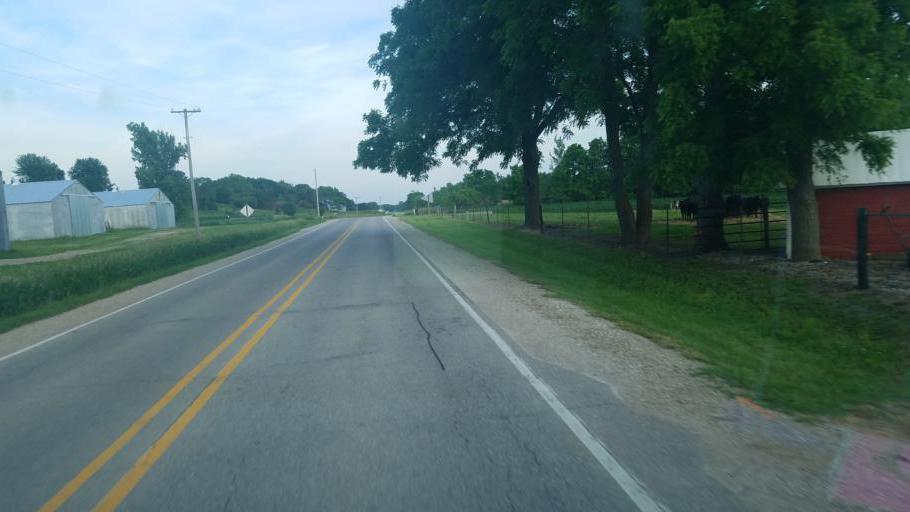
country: US
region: Iowa
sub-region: Benton County
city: Belle Plaine
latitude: 41.9326
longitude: -92.3993
